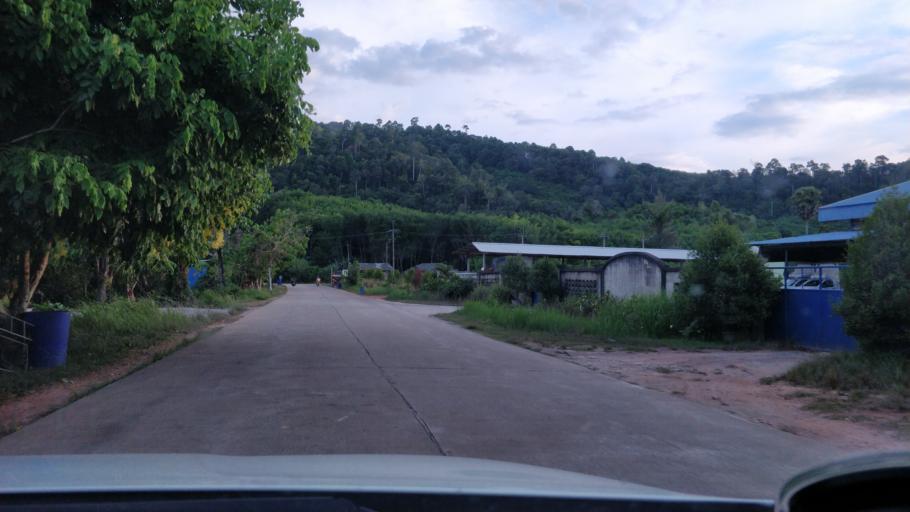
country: TH
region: Krabi
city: Saladan
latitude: 7.5832
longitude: 99.0678
